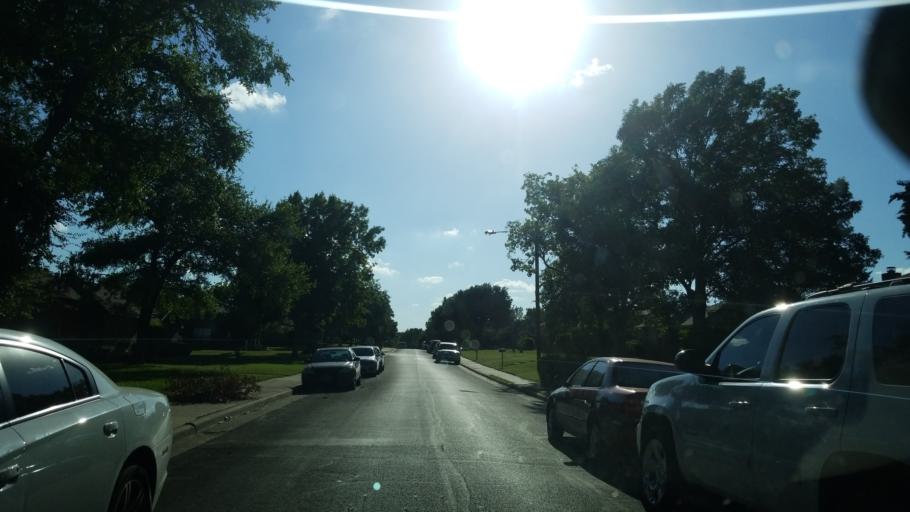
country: US
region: Texas
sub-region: Dallas County
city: Balch Springs
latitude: 32.7829
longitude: -96.7012
